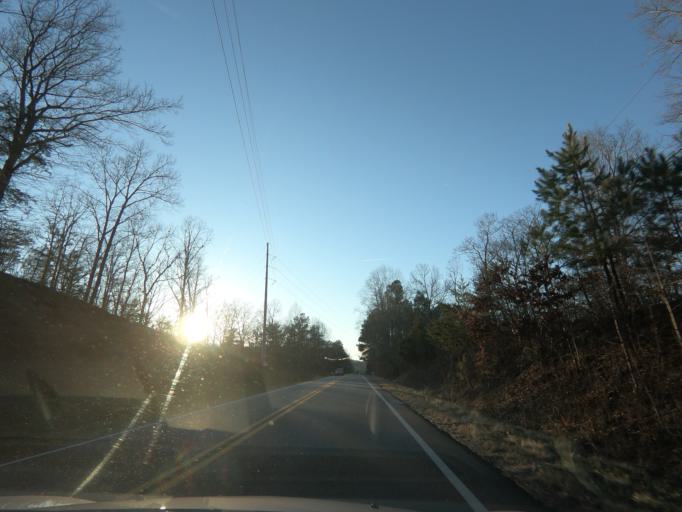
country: US
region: Georgia
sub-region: Dawson County
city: Dawsonville
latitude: 34.3540
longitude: -84.0847
